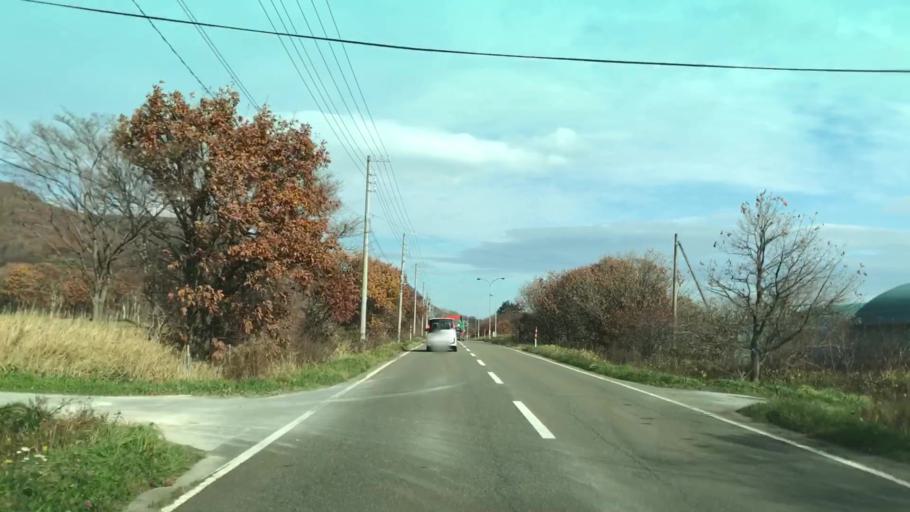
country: JP
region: Hokkaido
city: Obihiro
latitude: 42.0199
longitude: 143.2579
